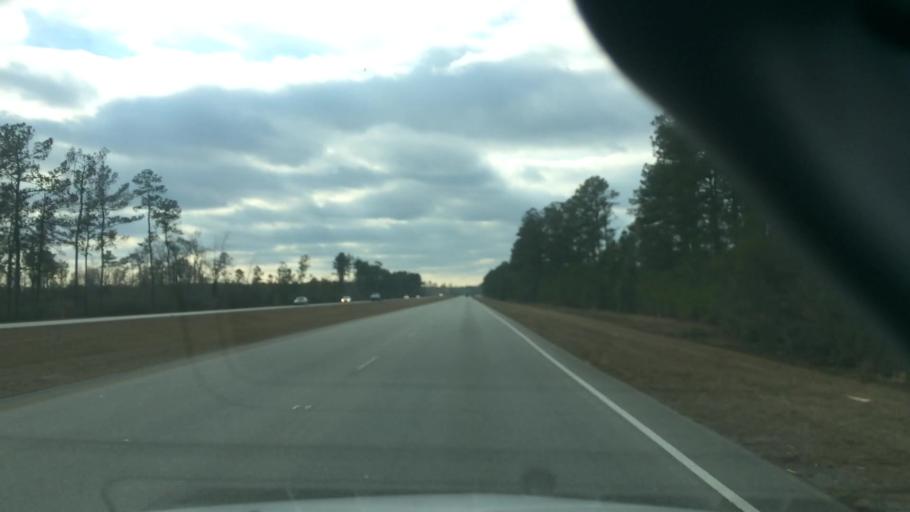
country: US
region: North Carolina
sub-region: Brunswick County
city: Bolivia
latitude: 34.0581
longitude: -78.2079
